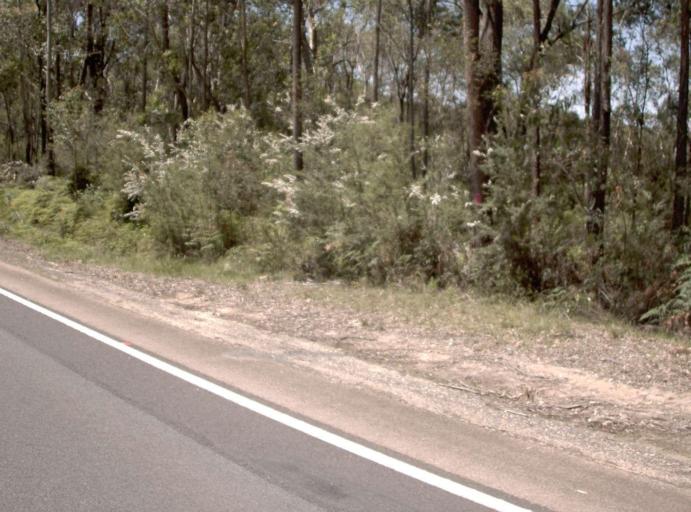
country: AU
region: Victoria
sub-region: East Gippsland
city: Lakes Entrance
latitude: -37.6900
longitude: 148.7500
